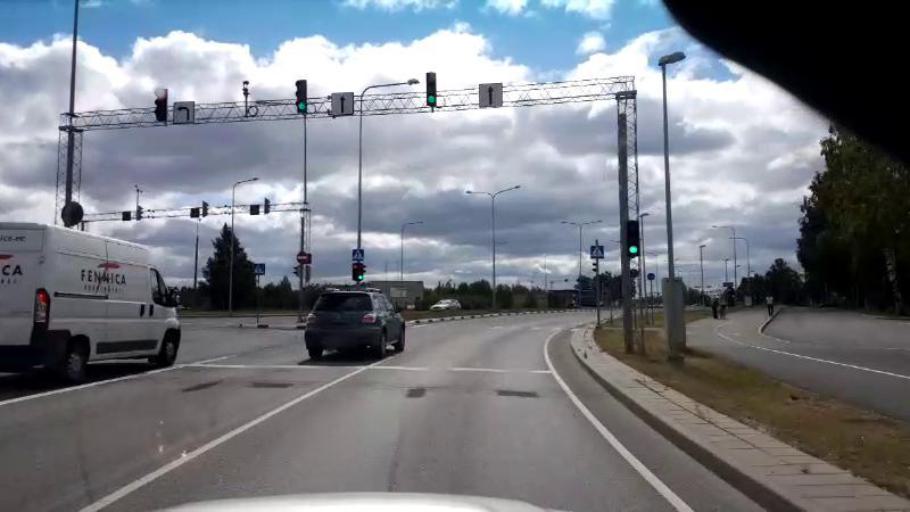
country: EE
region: Paernumaa
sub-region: Sauga vald
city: Sauga
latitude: 58.4070
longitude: 24.4977
